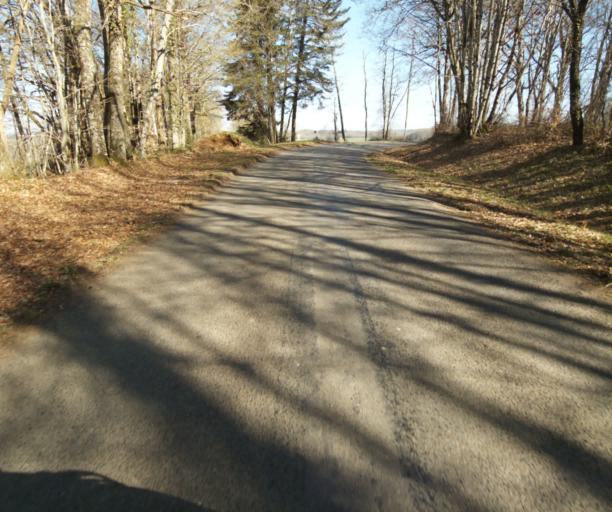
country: FR
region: Limousin
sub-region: Departement de la Correze
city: Seilhac
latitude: 45.3986
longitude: 1.7476
